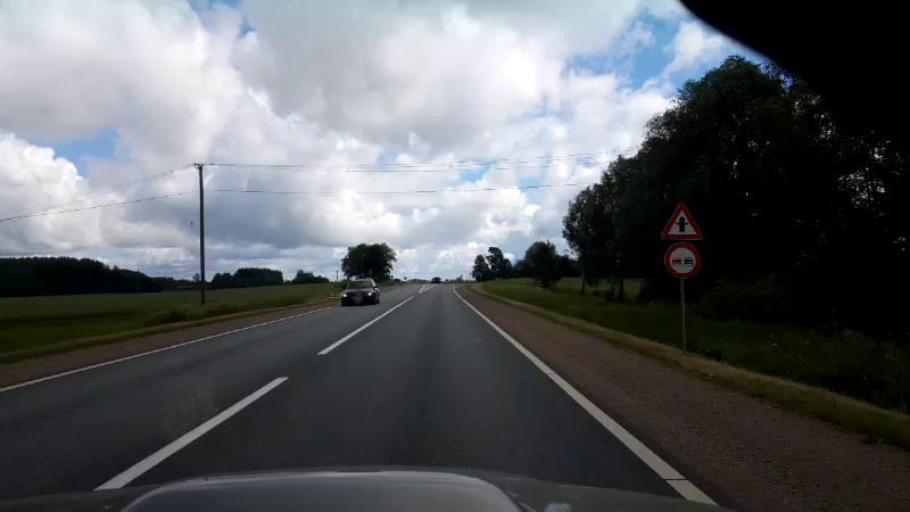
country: LV
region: Bauskas Rajons
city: Bauska
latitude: 56.4780
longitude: 24.1729
